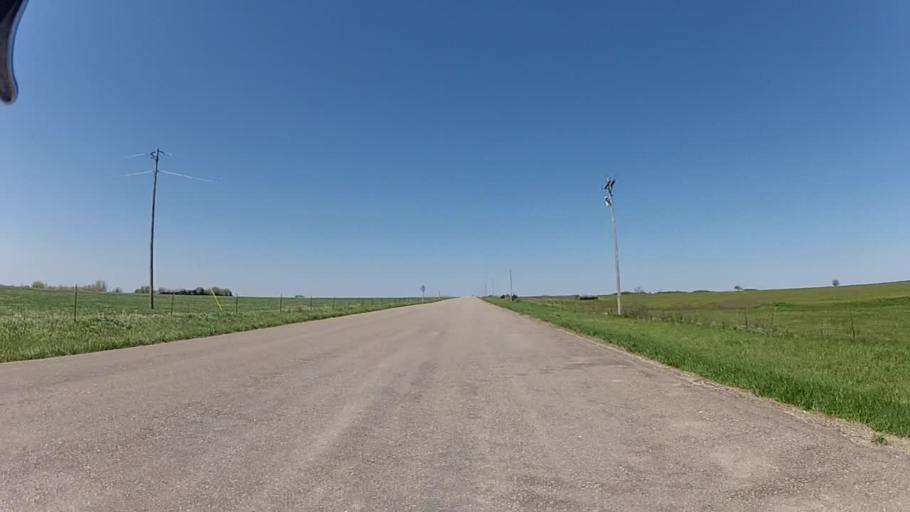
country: US
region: Kansas
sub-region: Riley County
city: Manhattan
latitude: 38.9714
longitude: -96.5211
